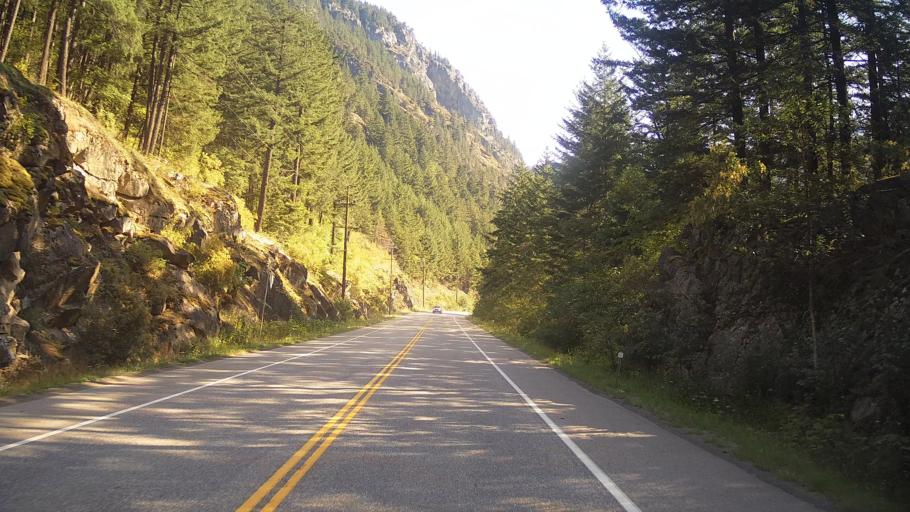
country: CA
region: British Columbia
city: Hope
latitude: 49.6133
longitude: -121.4120
